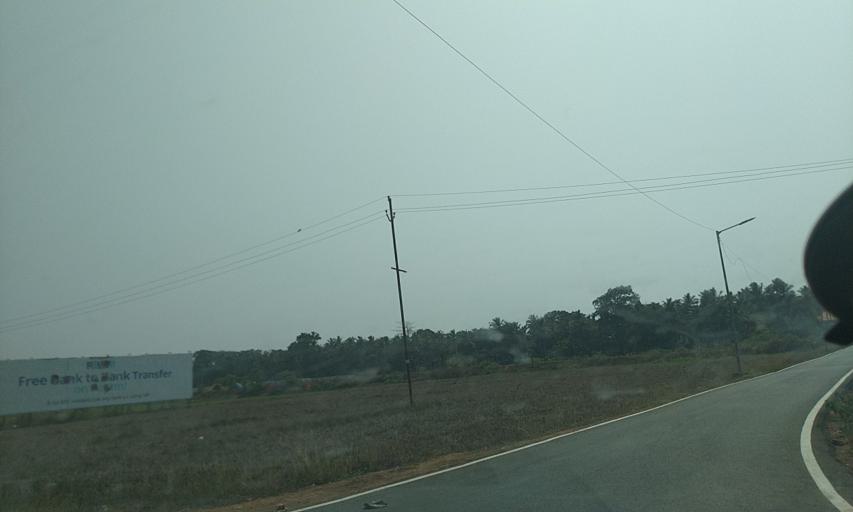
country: IN
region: Goa
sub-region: South Goa
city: Raia
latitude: 15.3019
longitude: 73.9492
